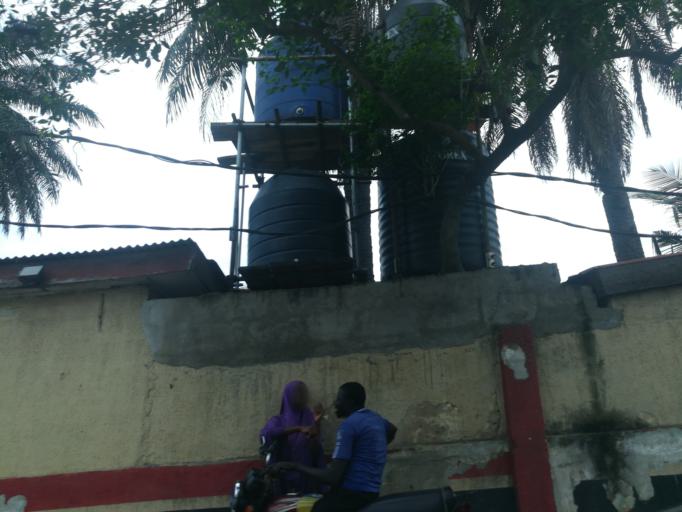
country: NG
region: Lagos
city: Ojota
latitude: 6.5647
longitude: 3.3654
